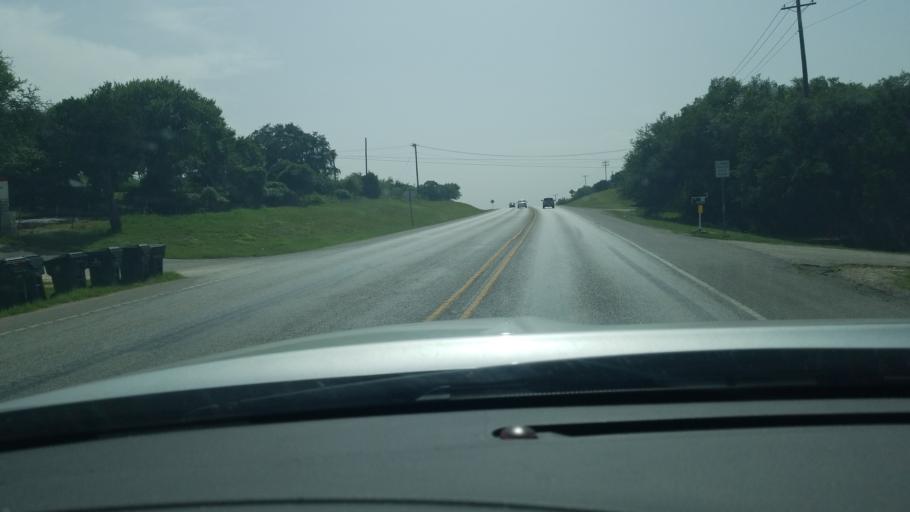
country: US
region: Texas
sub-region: Comal County
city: Bulverde
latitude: 29.7970
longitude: -98.4525
